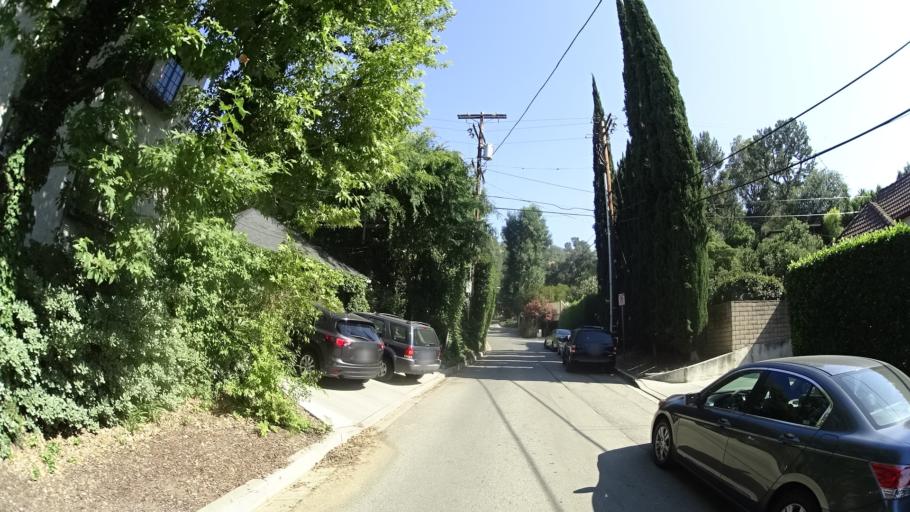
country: US
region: California
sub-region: Los Angeles County
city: Universal City
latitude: 34.1389
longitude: -118.3754
